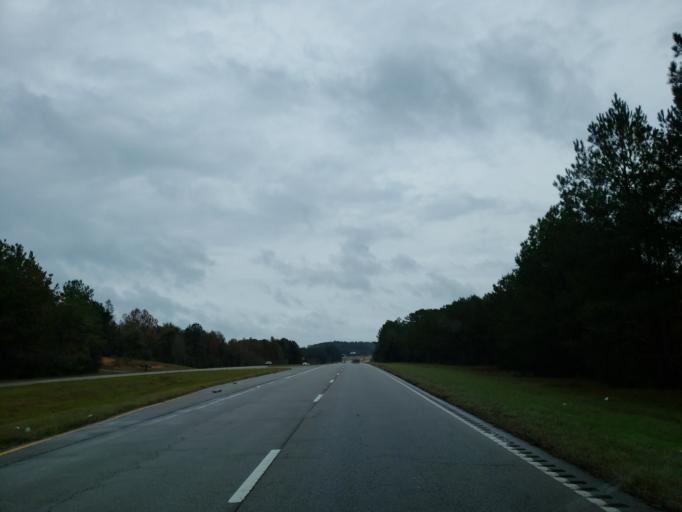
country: US
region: Mississippi
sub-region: Jones County
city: Laurel
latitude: 31.7039
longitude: -89.0797
